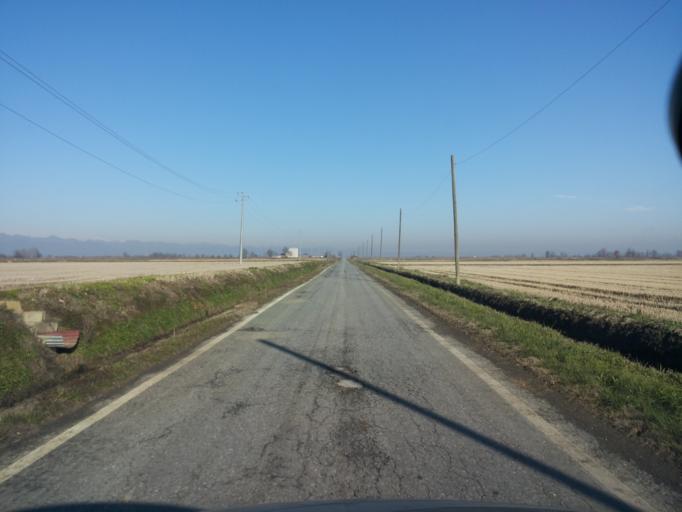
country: IT
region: Piedmont
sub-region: Provincia di Vercelli
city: Formigliana
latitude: 45.4122
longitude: 8.2483
